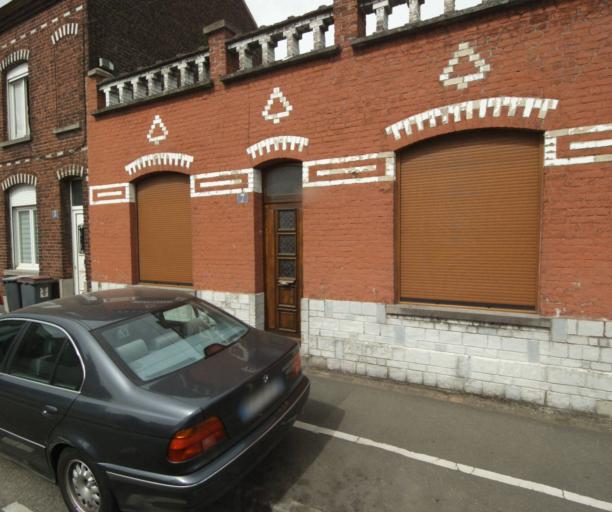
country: FR
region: Nord-Pas-de-Calais
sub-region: Departement du Nord
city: Wattrelos
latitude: 50.6906
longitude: 3.2067
